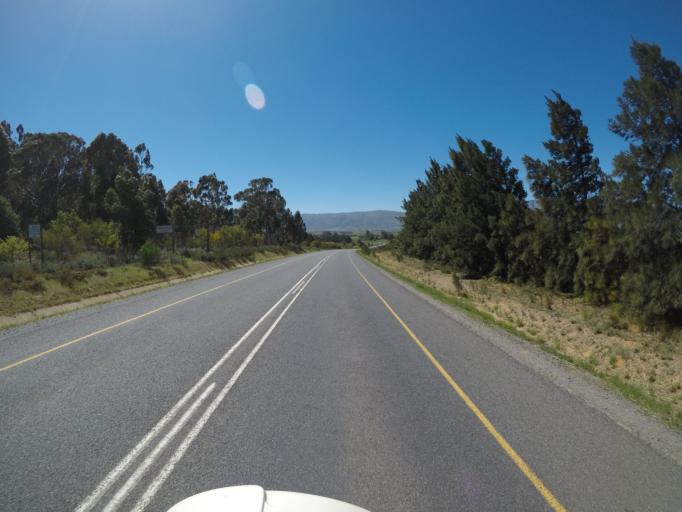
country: ZA
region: Western Cape
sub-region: Cape Winelands District Municipality
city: Ceres
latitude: -33.3126
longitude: 19.0960
